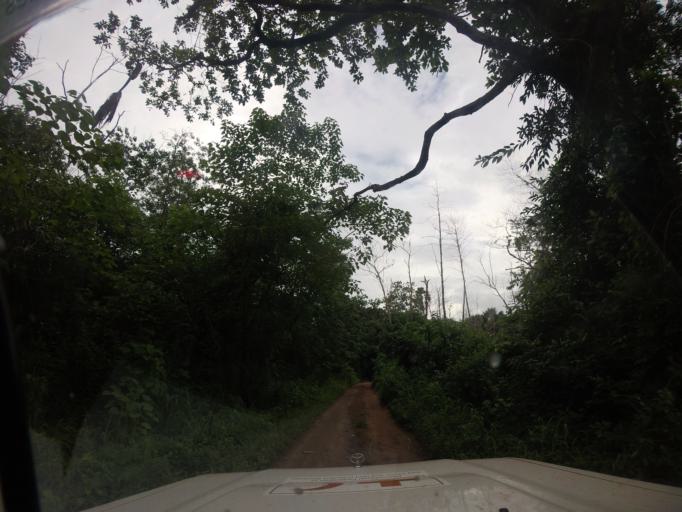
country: SL
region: Northern Province
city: Kamakwie
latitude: 9.6435
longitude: -12.2150
